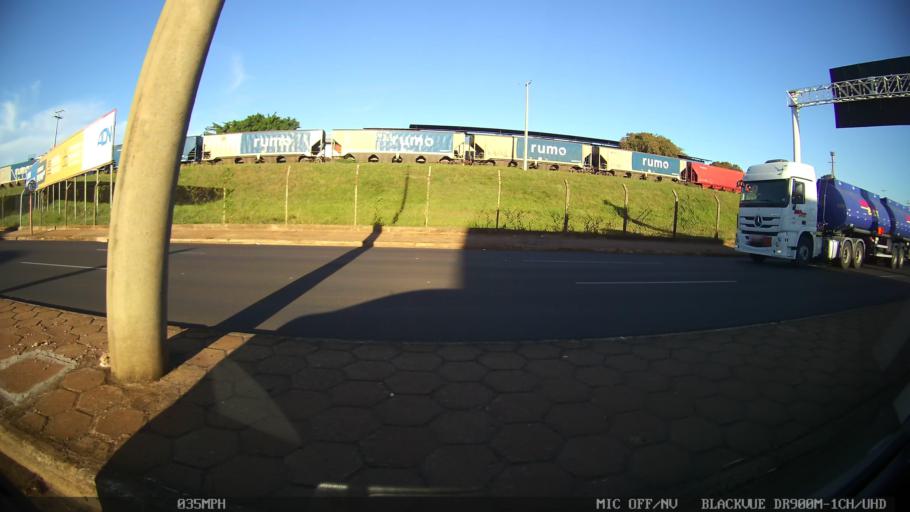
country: BR
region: Sao Paulo
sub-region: Araraquara
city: Araraquara
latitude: -21.7809
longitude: -48.1706
